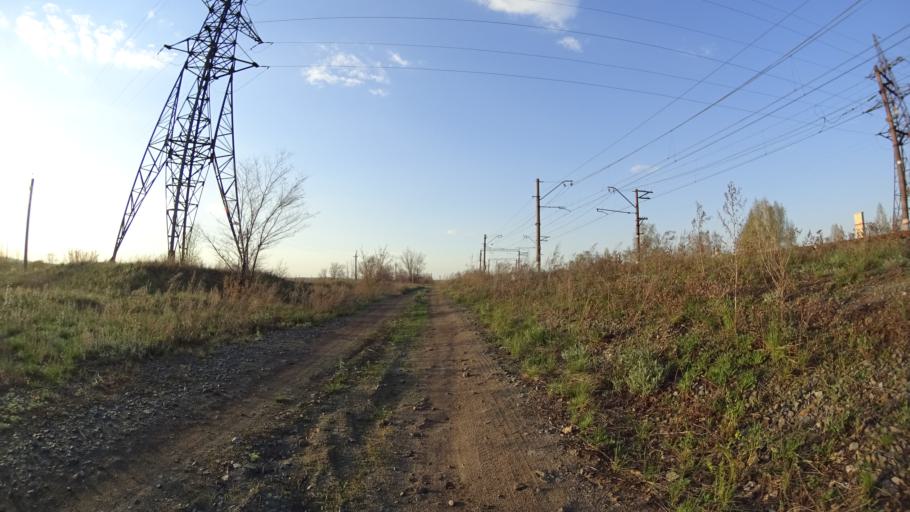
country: RU
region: Chelyabinsk
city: Troitsk
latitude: 54.0608
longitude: 61.6137
